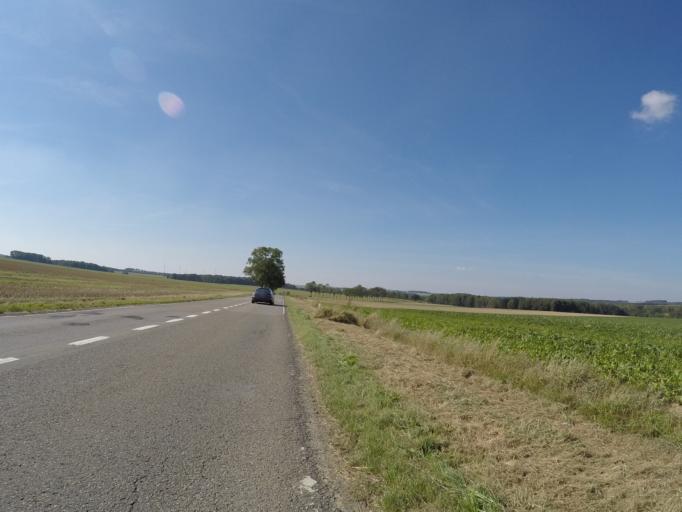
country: BE
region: Wallonia
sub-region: Province de Namur
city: Ciney
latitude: 50.3130
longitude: 5.0496
